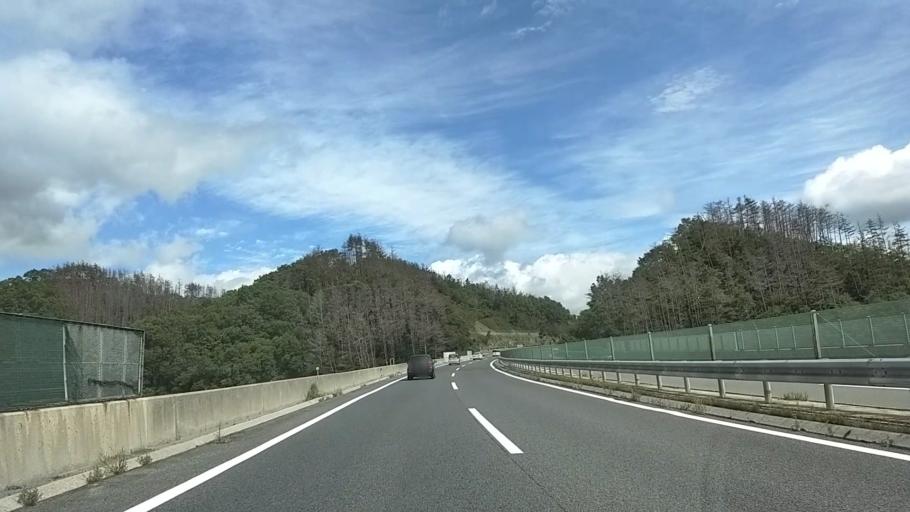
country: JP
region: Nagano
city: Hotaka
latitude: 36.4323
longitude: 138.0112
